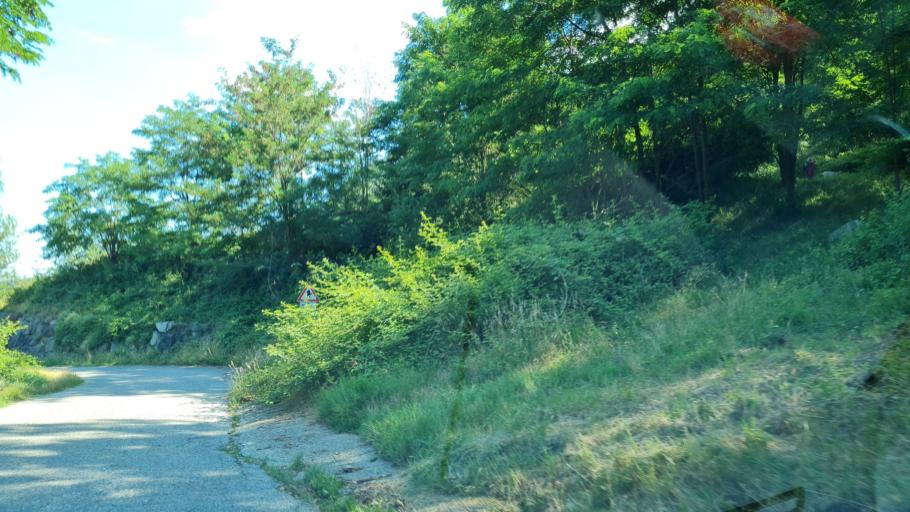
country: IT
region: Piedmont
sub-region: Provincia di Torino
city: Quincinetto
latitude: 45.5555
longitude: 7.8073
